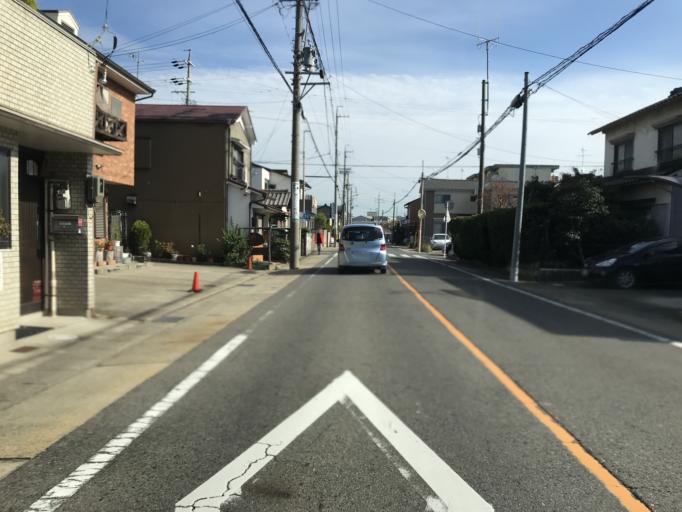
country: JP
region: Aichi
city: Kasugai
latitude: 35.2205
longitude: 136.9367
